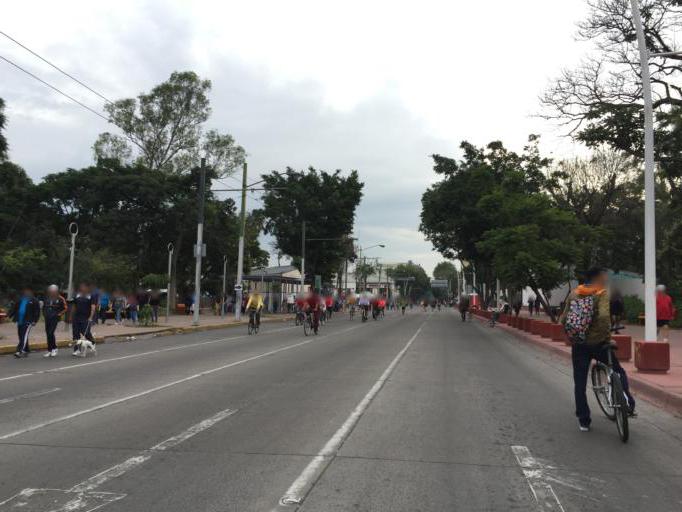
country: MX
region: Jalisco
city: Guadalajara
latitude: 20.6749
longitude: -103.3563
